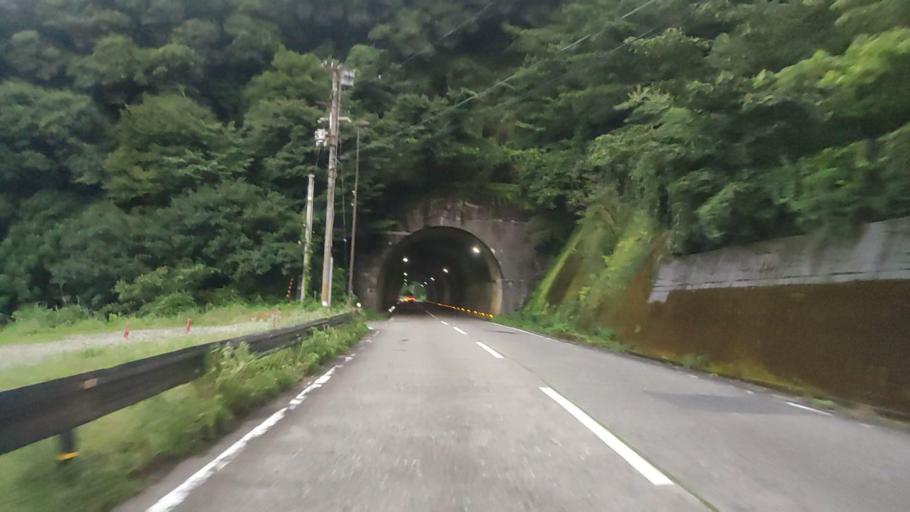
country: JP
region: Wakayama
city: Shingu
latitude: 33.7568
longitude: 135.9211
